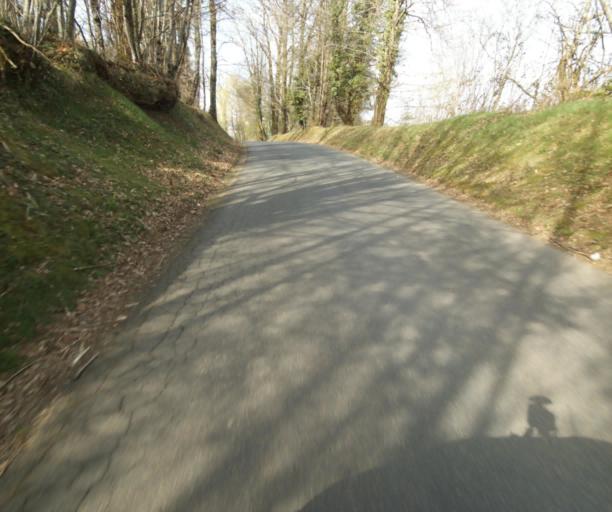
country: FR
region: Limousin
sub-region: Departement de la Correze
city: Naves
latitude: 45.3320
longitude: 1.7569
